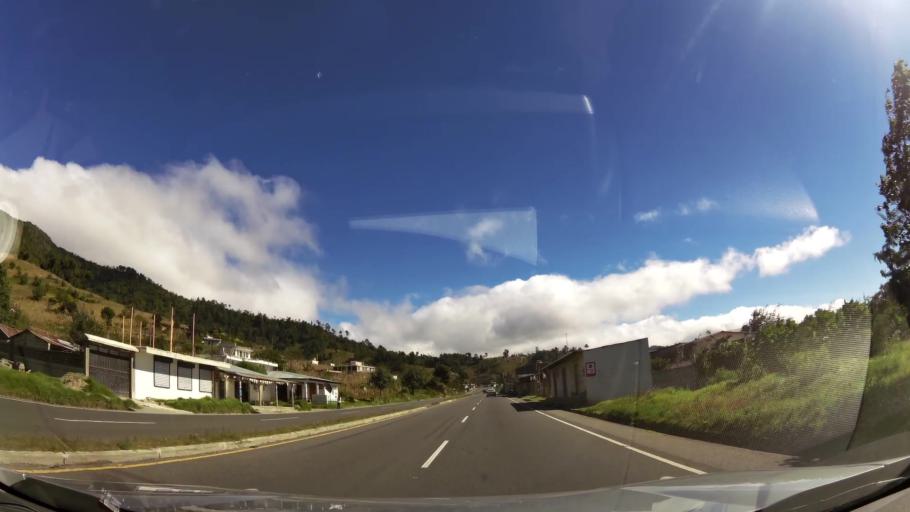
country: GT
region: Solola
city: Solola
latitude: 14.8251
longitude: -91.1975
